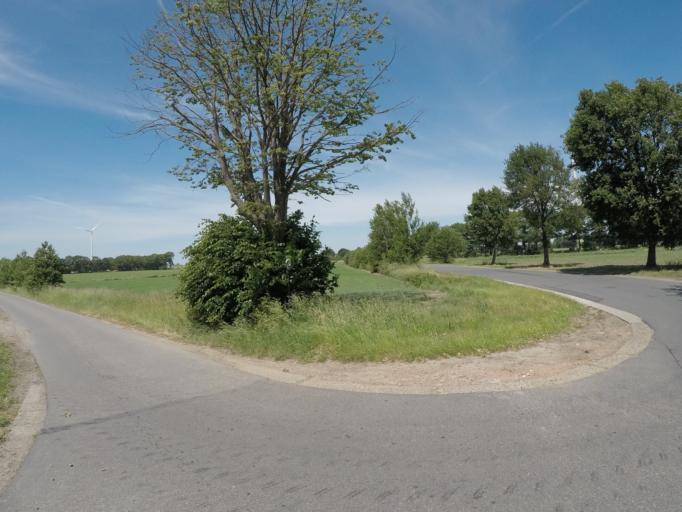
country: BE
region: Flanders
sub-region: Provincie Antwerpen
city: Hoogstraten
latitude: 51.4103
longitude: 4.7115
